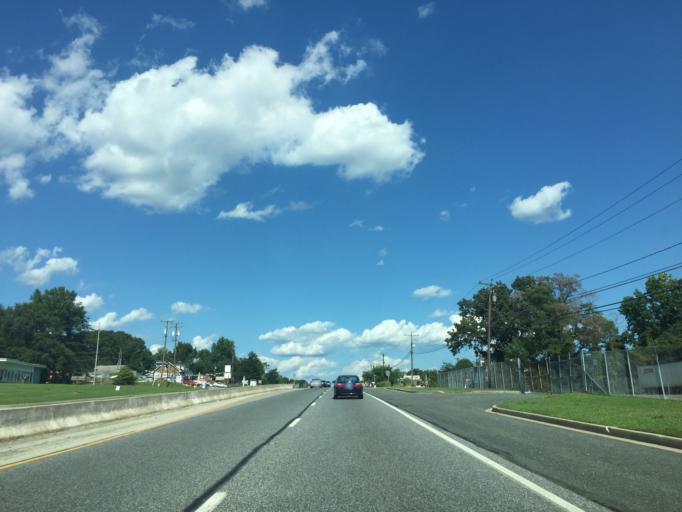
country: US
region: Maryland
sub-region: Harford County
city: Joppatowne
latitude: 39.4304
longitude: -76.3467
